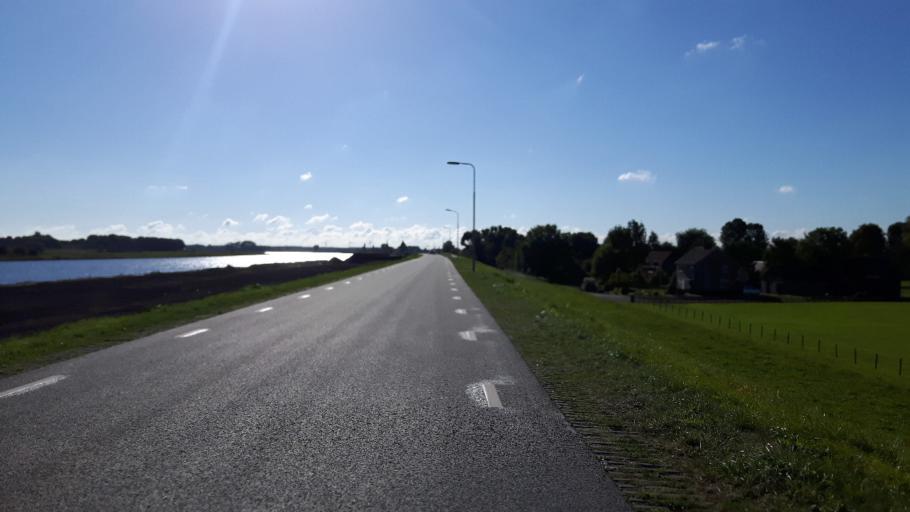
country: NL
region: Utrecht
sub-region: Gemeente Vianen
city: Vianen
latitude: 51.9814
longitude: 5.1407
